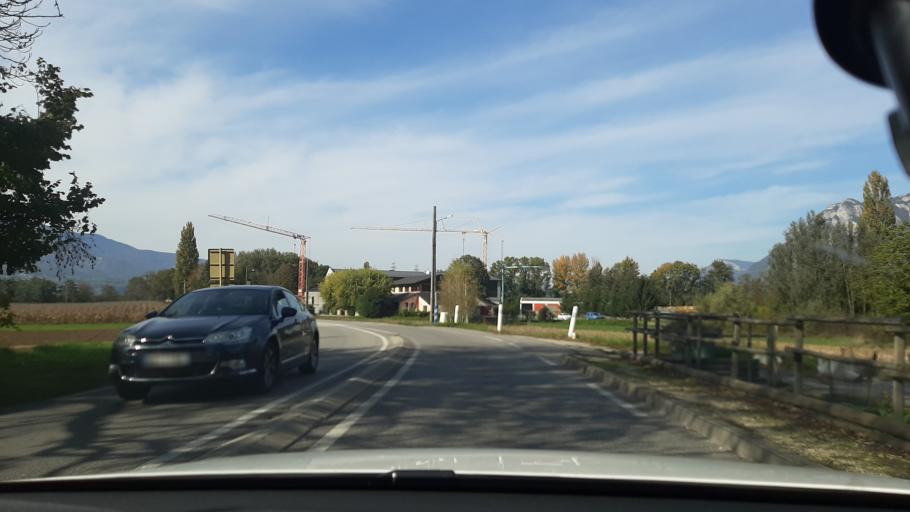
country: FR
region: Rhone-Alpes
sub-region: Departement de la Savoie
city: Montmelian
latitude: 45.4610
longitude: 6.0512
